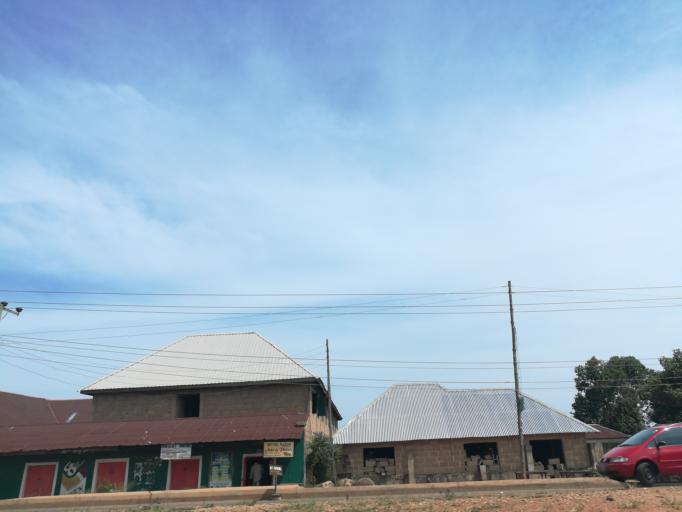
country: NG
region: Plateau
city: Bukuru
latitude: 9.7661
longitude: 8.8599
